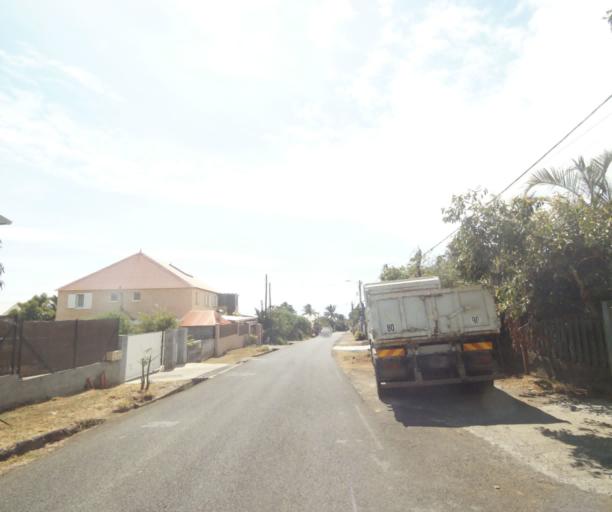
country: RE
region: Reunion
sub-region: Reunion
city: Saint-Paul
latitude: -21.0589
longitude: 55.2590
